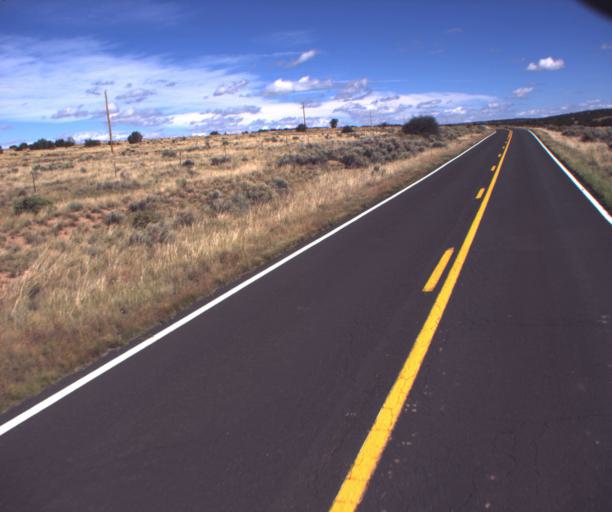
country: US
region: Arizona
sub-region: Apache County
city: Houck
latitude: 34.9380
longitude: -109.1832
